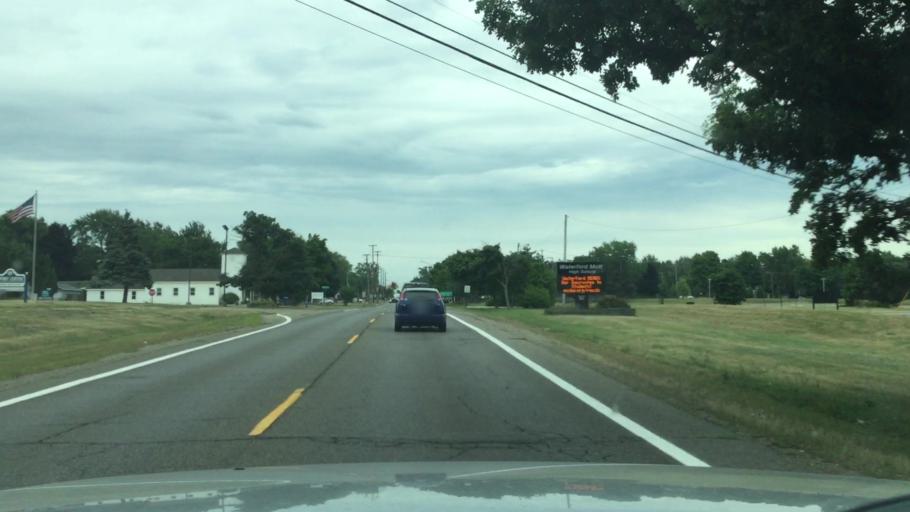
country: US
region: Michigan
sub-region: Oakland County
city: Keego Harbor
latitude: 42.6571
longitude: -83.3466
